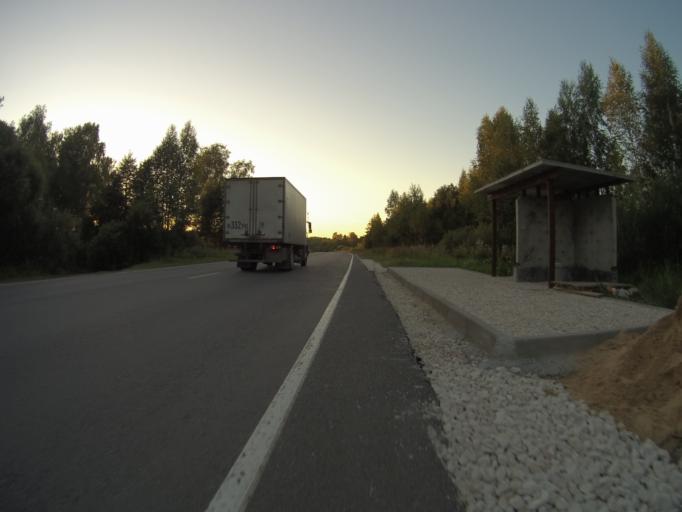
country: RU
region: Vladimir
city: Anopino
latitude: 55.8201
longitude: 40.6608
